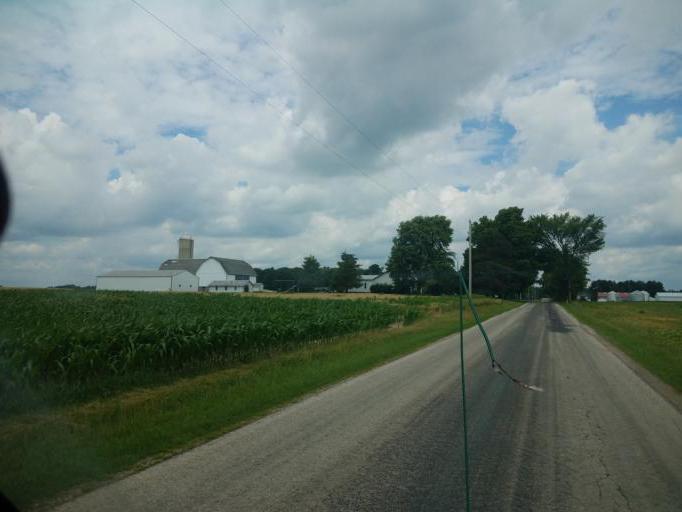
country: US
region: Ohio
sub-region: Richland County
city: Shelby
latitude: 40.9316
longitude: -82.7049
